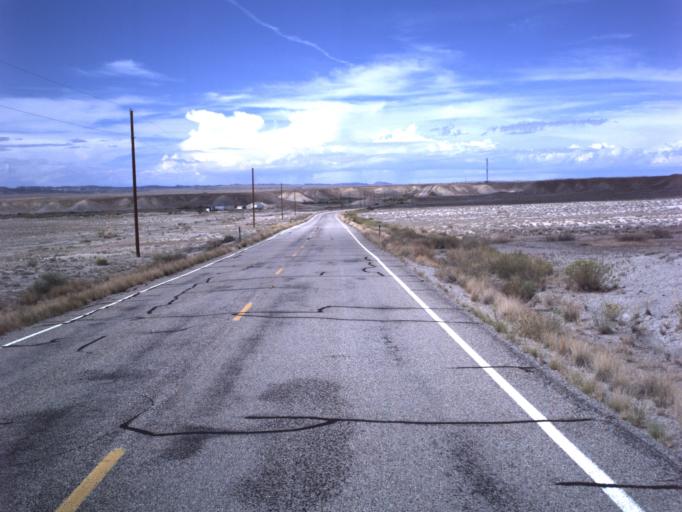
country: US
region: Utah
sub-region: Grand County
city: Moab
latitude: 38.9398
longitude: -109.3848
